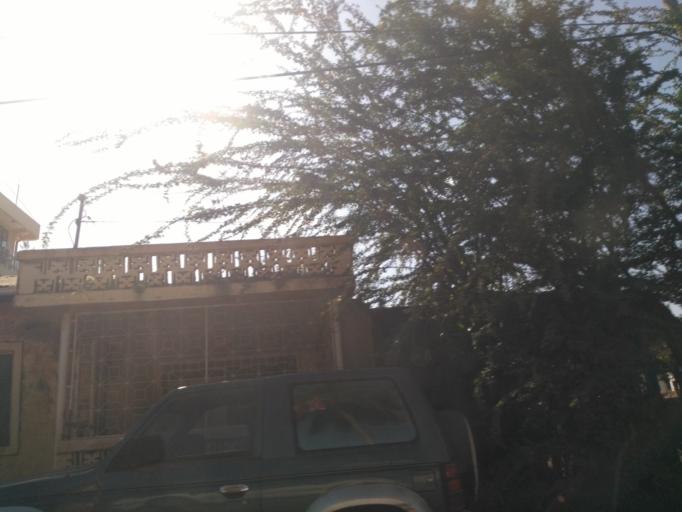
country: TZ
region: Mwanza
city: Mwanza
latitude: -2.5052
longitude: 32.8987
